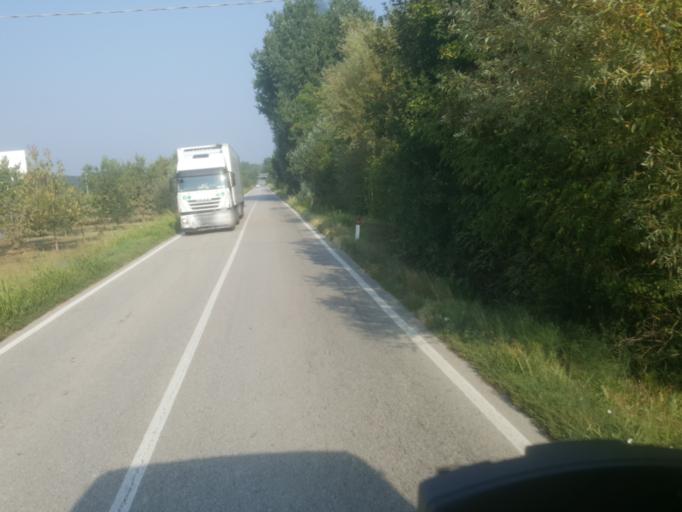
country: IT
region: Emilia-Romagna
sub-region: Provincia di Ravenna
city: Lavezzola
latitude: 44.5720
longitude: 11.8847
